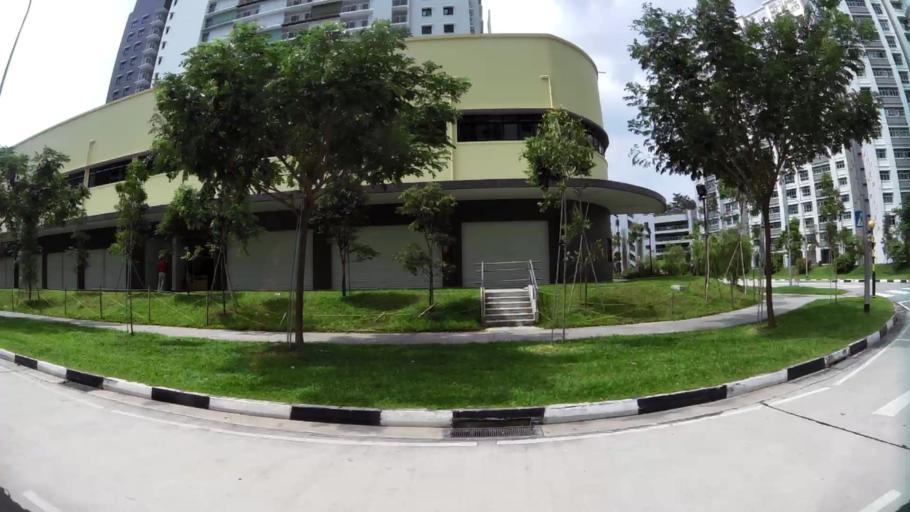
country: SG
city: Singapore
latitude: 1.3554
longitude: 103.9318
